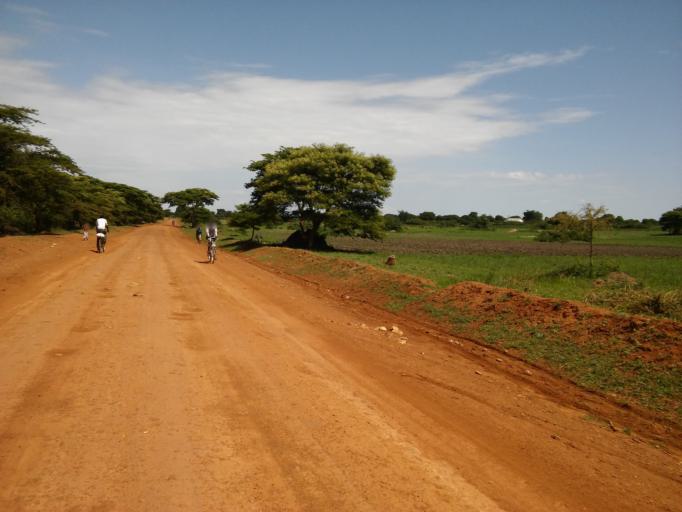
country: UG
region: Eastern Region
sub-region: Kumi District
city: Kumi
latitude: 1.4843
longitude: 33.9133
